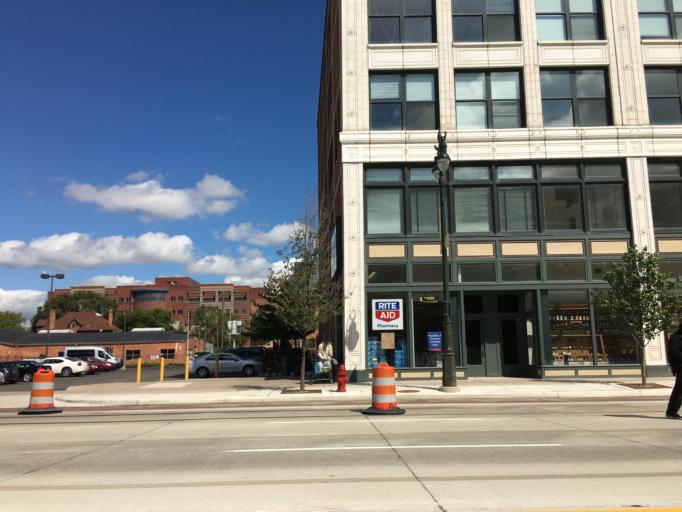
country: US
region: Michigan
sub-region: Wayne County
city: Detroit
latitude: 42.3540
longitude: -83.0625
